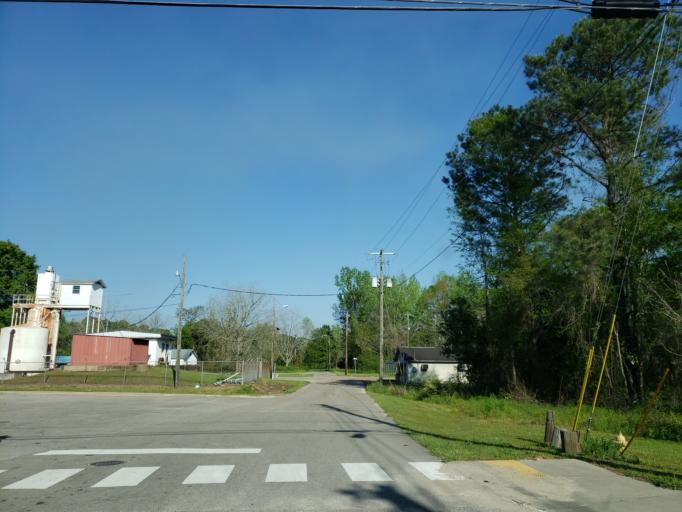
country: US
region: Mississippi
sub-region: Perry County
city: Richton
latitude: 31.3470
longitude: -88.9360
